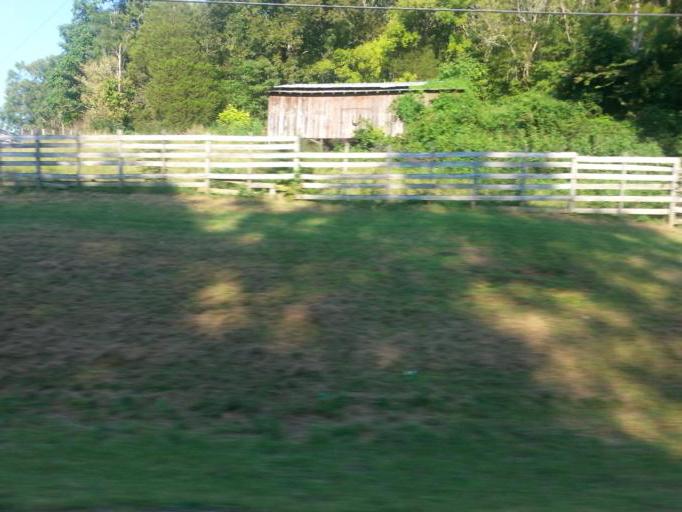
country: US
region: Tennessee
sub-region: Sevier County
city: Seymour
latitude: 35.9393
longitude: -83.8128
